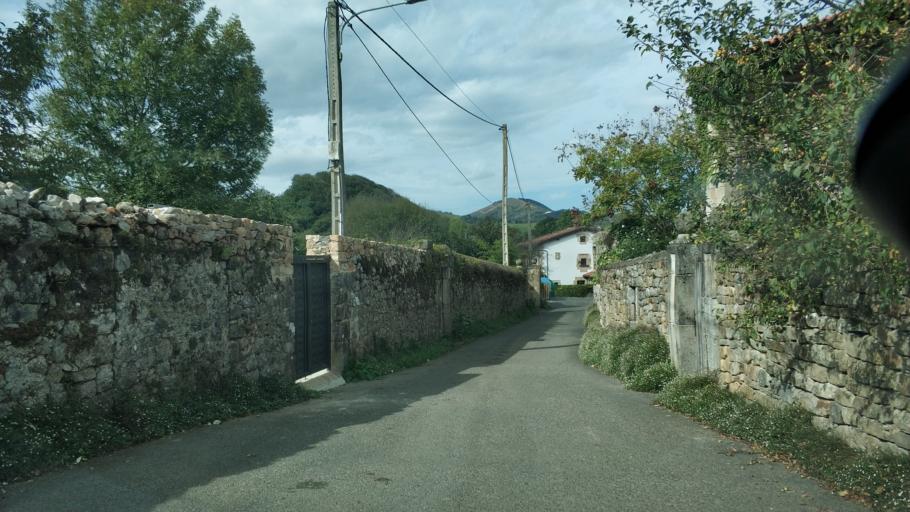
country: ES
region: Cantabria
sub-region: Provincia de Cantabria
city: Santa Maria de Cayon
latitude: 43.2814
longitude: -3.8023
